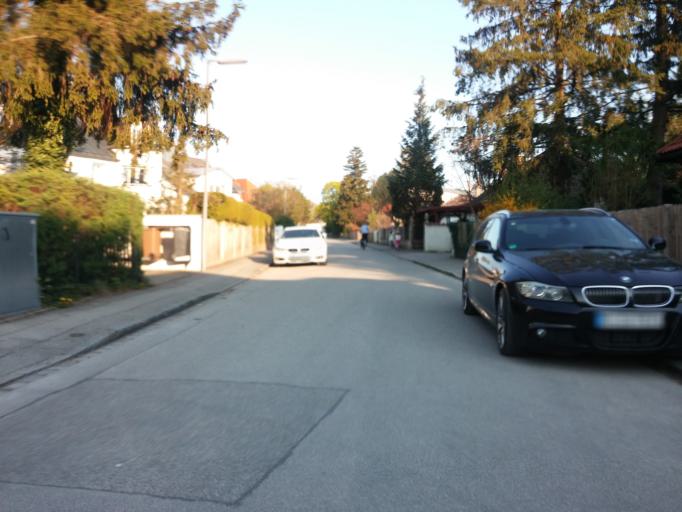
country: DE
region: Bavaria
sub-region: Upper Bavaria
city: Haar
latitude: 48.1109
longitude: 11.6937
